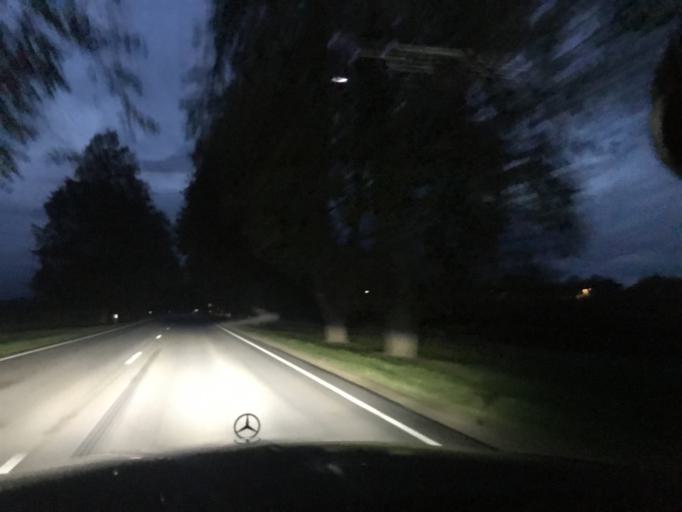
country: EE
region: Valgamaa
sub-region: Torva linn
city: Torva
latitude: 58.0118
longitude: 25.8909
